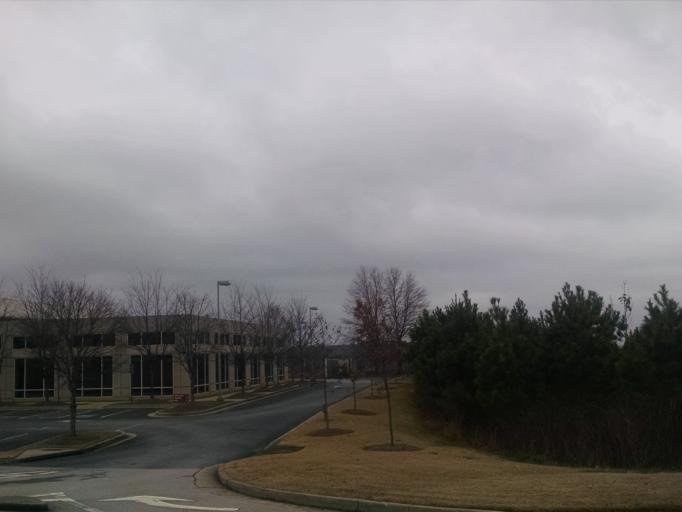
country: US
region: Georgia
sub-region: Gwinnett County
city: Sugar Hill
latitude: 34.0979
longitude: -84.0155
